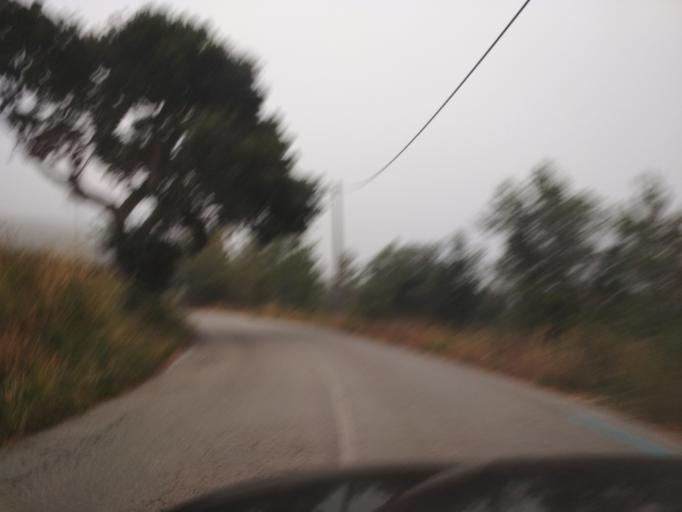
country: PT
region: Coimbra
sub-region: Coimbra
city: Coimbra
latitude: 40.1859
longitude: -8.4356
